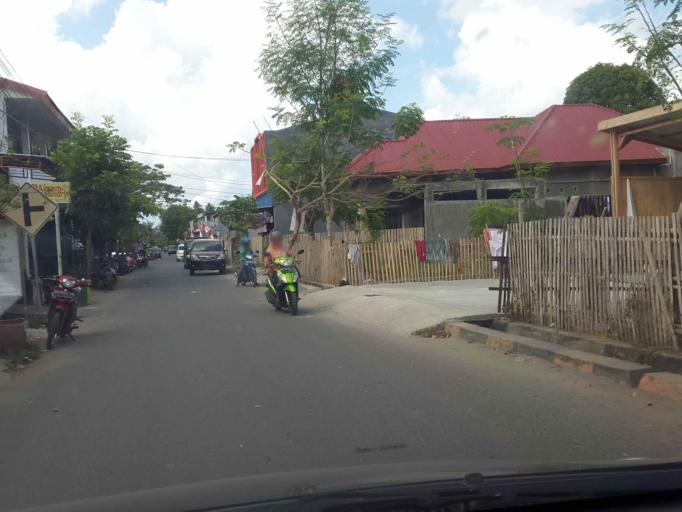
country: ID
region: South Sulawesi
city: Bantaeng
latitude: -6.1197
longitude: 120.4637
